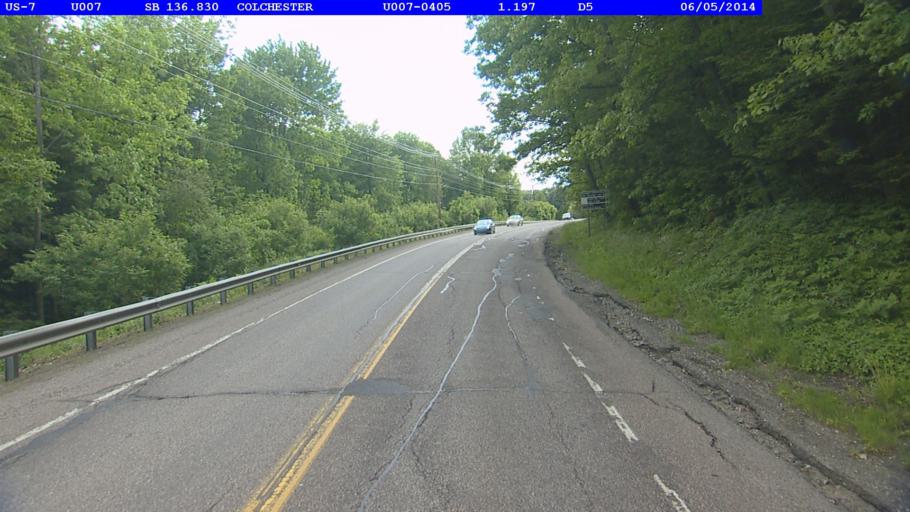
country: US
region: Vermont
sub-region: Chittenden County
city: Winooski
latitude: 44.5181
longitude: -73.1755
